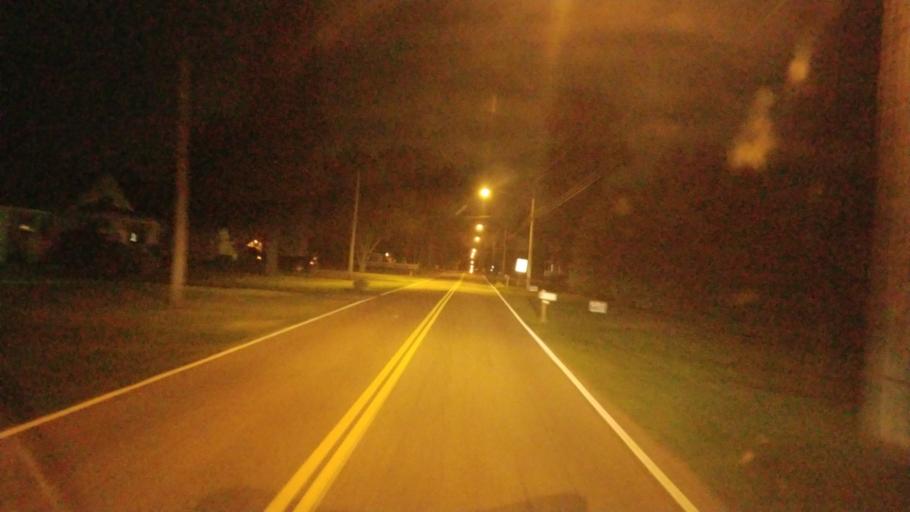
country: US
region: Ohio
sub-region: Stark County
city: Massillon
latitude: 40.7625
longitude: -81.5462
